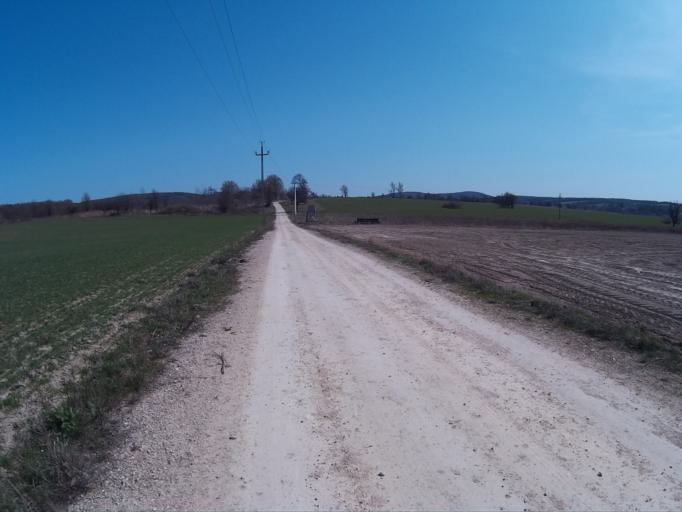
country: HU
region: Veszprem
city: Herend
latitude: 47.2047
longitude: 17.7830
